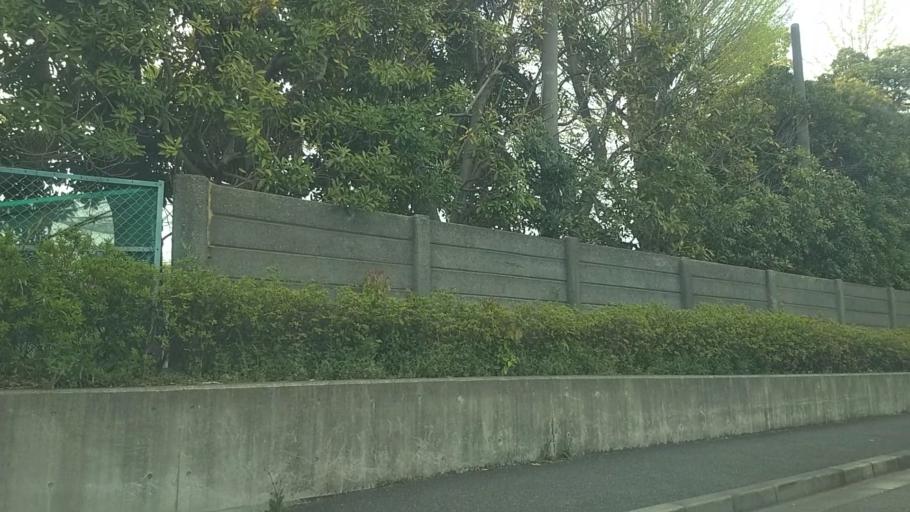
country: JP
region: Kanagawa
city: Kamakura
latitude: 35.3661
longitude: 139.5555
